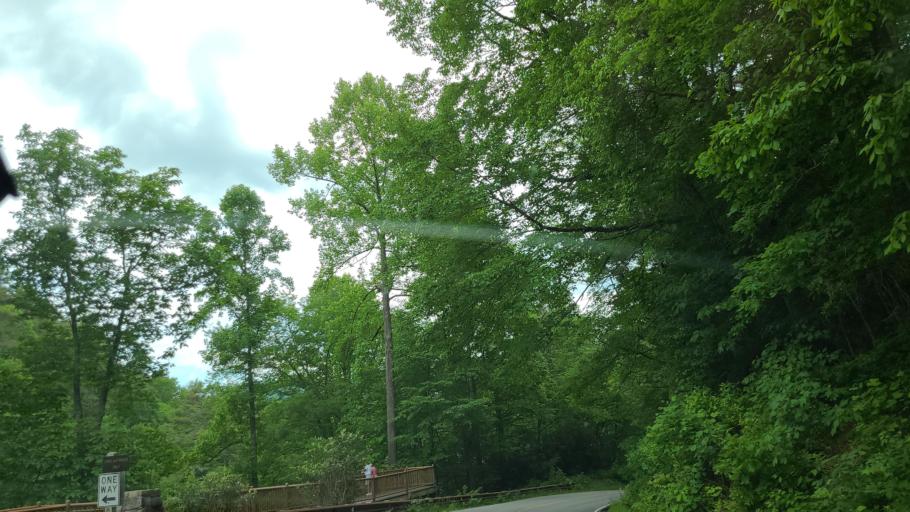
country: US
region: North Carolina
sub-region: Macon County
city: Franklin
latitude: 35.0685
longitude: -83.2383
